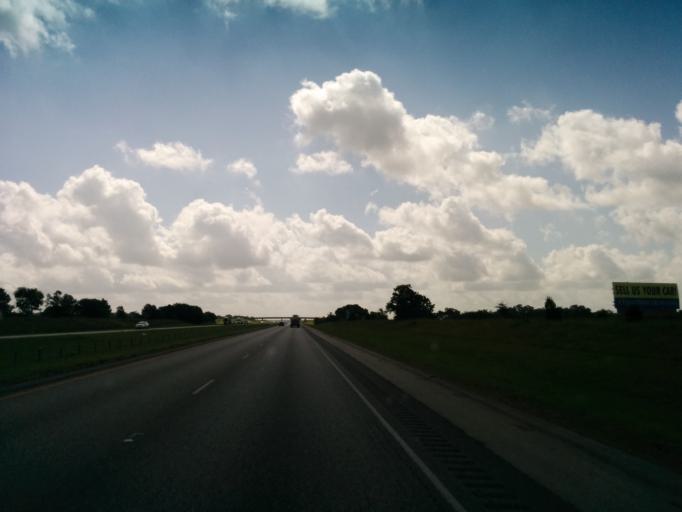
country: US
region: Texas
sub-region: Fayette County
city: Schulenburg
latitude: 29.6905
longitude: -96.9750
